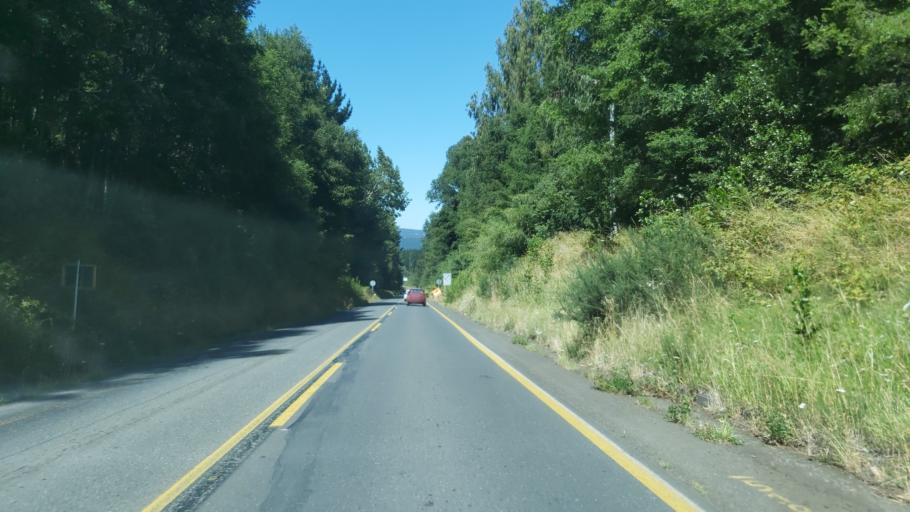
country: CL
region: Araucania
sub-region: Provincia de Cautin
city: Vilcun
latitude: -38.4156
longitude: -71.9450
